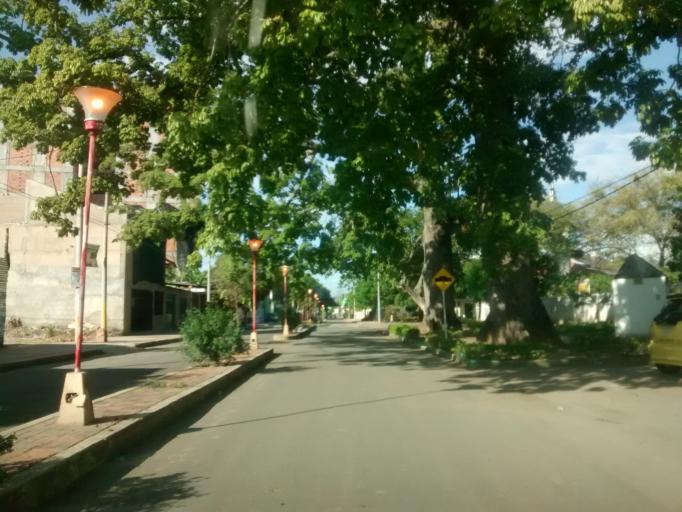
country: CO
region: Cundinamarca
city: Ricaurte
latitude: 4.2791
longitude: -74.7695
